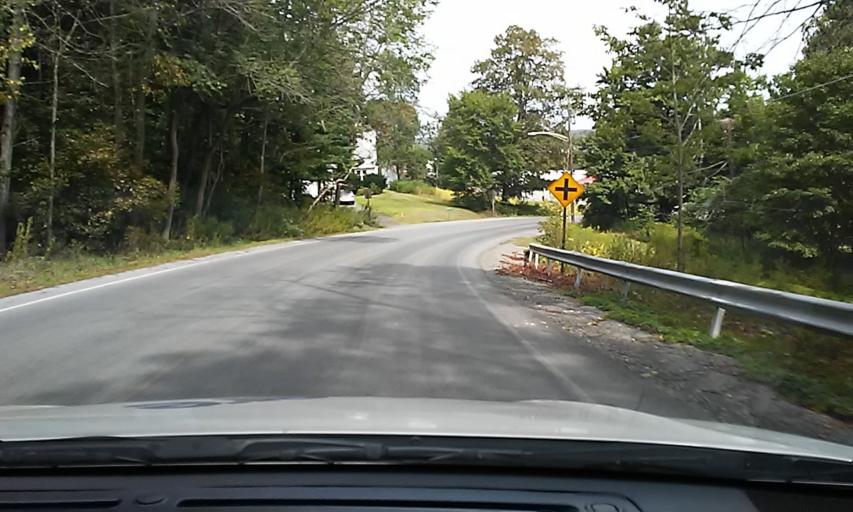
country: US
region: Pennsylvania
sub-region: Elk County
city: Saint Marys
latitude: 41.3520
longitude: -78.6075
